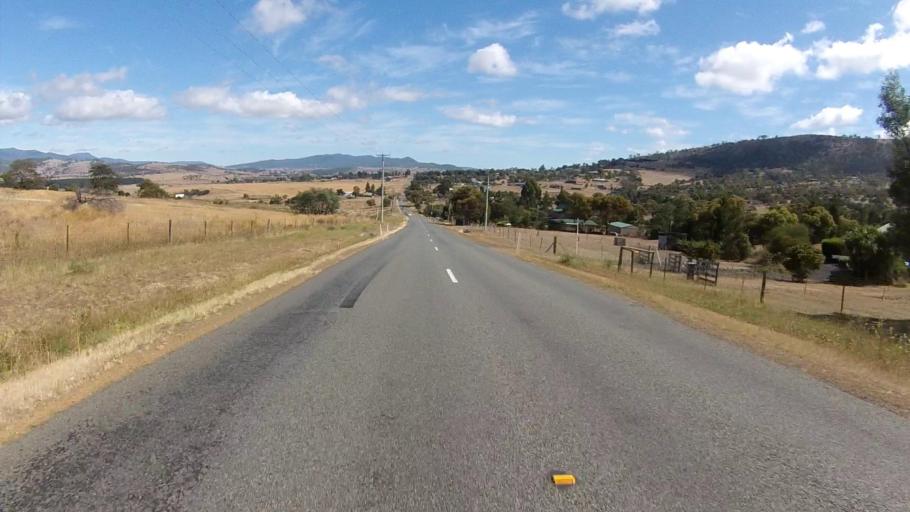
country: AU
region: Tasmania
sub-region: Glenorchy
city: Austins Ferry
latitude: -42.7260
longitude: 147.2849
